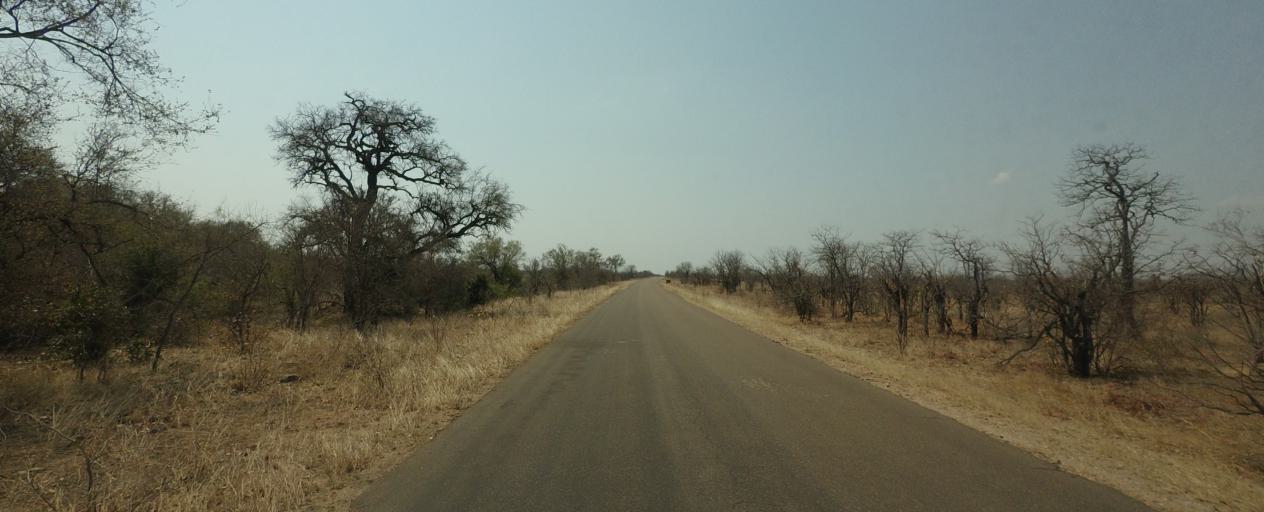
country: ZA
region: Limpopo
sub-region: Mopani District Municipality
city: Phalaborwa
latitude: -23.3687
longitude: 31.3201
